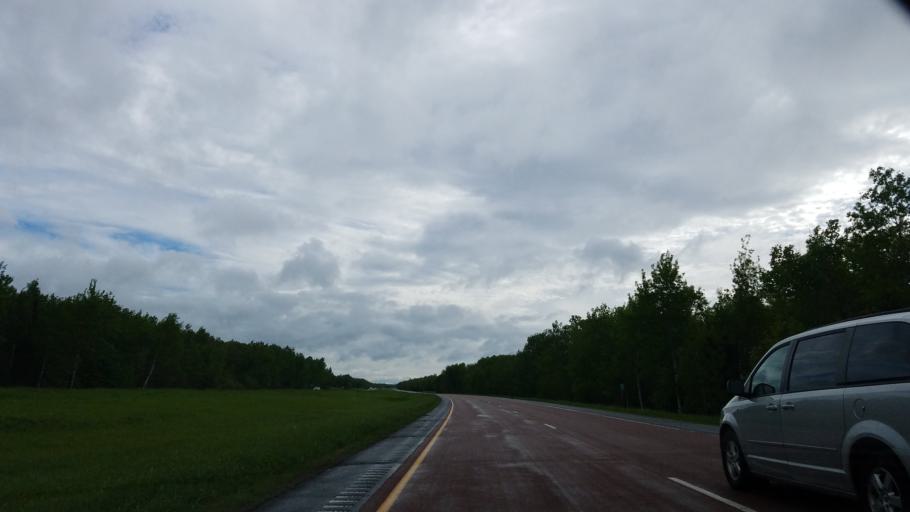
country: US
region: Minnesota
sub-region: Saint Louis County
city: Arnold
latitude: 46.8666
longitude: -91.9617
